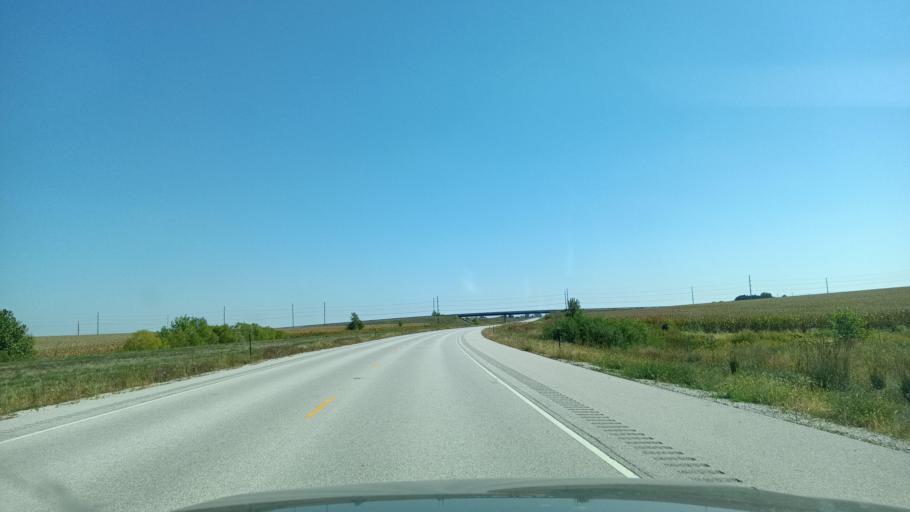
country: US
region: Illinois
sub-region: McDonough County
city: Macomb
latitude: 40.5030
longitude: -90.7003
